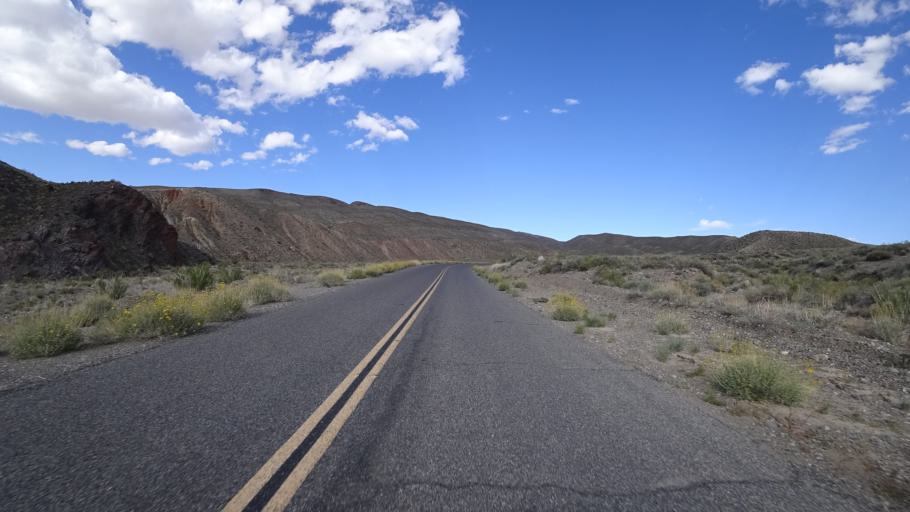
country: US
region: Nevada
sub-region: Nye County
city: Beatty
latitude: 36.4140
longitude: -117.1807
